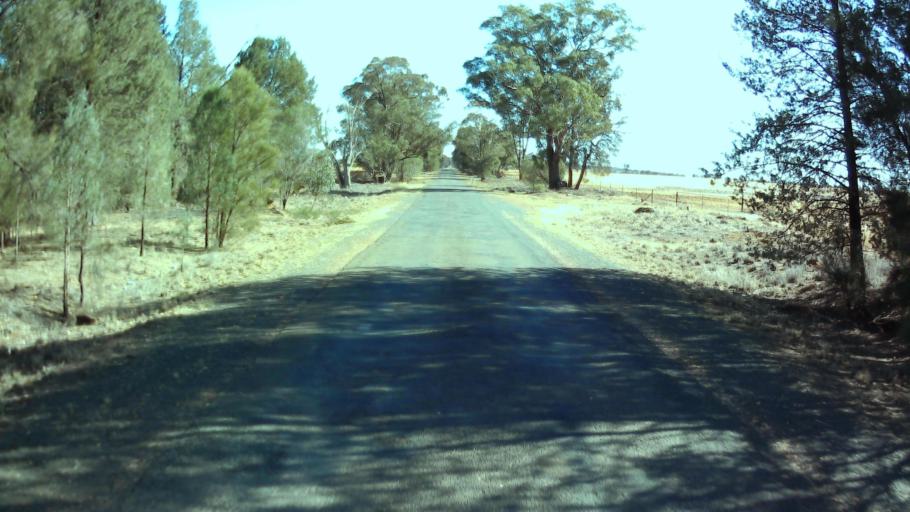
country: AU
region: New South Wales
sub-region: Weddin
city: Grenfell
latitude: -33.8074
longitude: 147.9546
